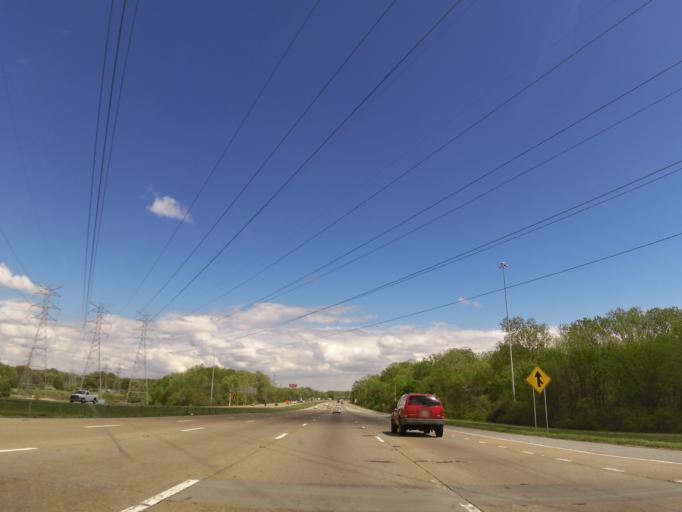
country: US
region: Tennessee
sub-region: Shelby County
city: Memphis
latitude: 35.1918
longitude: -90.0063
